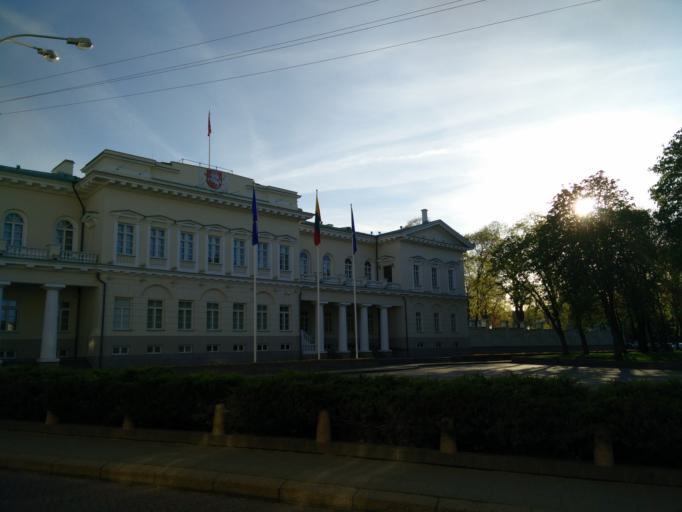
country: LT
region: Vilnius County
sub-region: Vilnius
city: Vilnius
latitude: 54.6836
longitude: 25.2868
